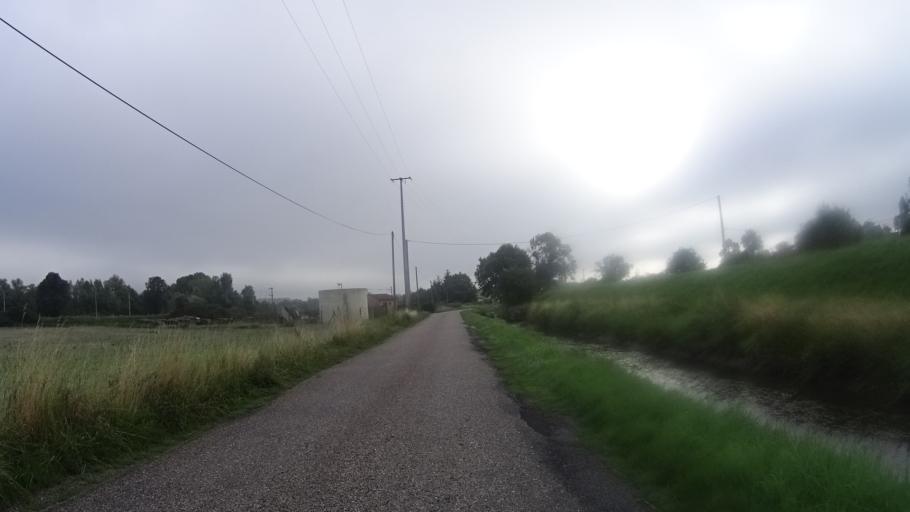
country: FR
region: Lorraine
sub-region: Departement de la Meuse
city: Fains-Veel
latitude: 48.8028
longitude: 5.0649
